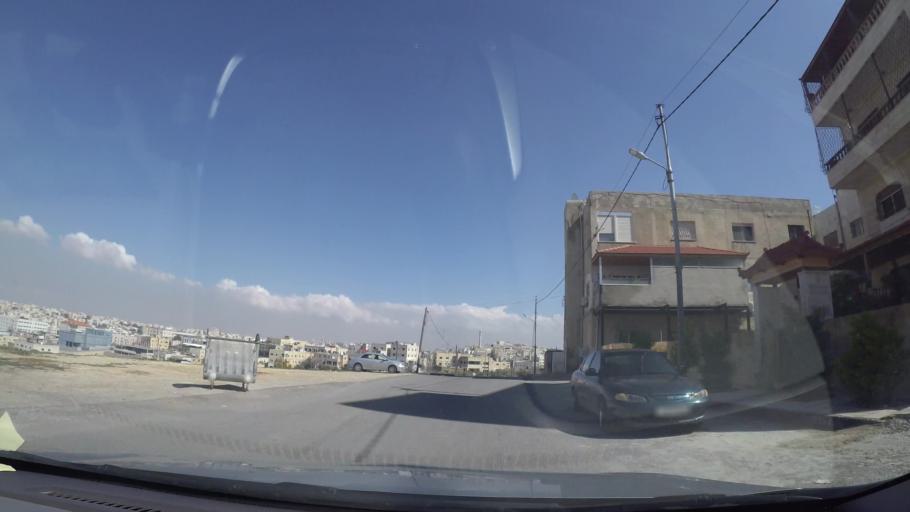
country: JO
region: Amman
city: Al Bunayyat ash Shamaliyah
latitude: 31.9086
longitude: 35.9075
